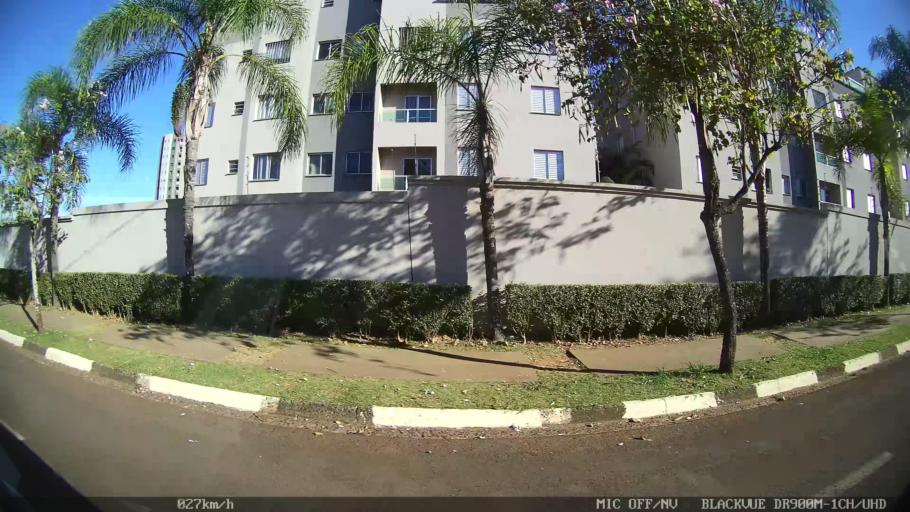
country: BR
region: Sao Paulo
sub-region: Franca
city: Franca
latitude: -20.5641
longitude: -47.4027
